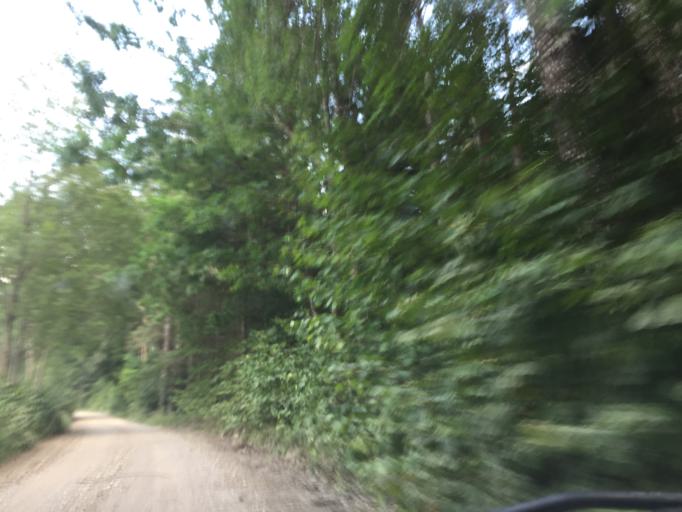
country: LT
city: Zagare
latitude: 56.4459
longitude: 23.1584
